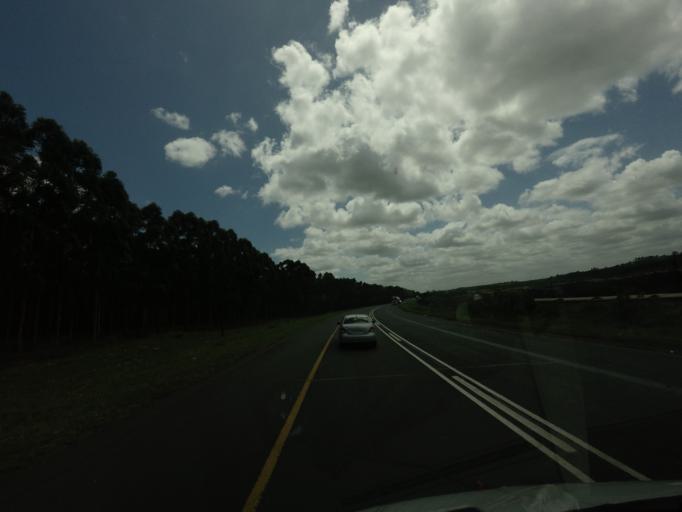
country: ZA
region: KwaZulu-Natal
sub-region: uThungulu District Municipality
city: KwaMbonambi
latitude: -28.5498
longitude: 32.1195
